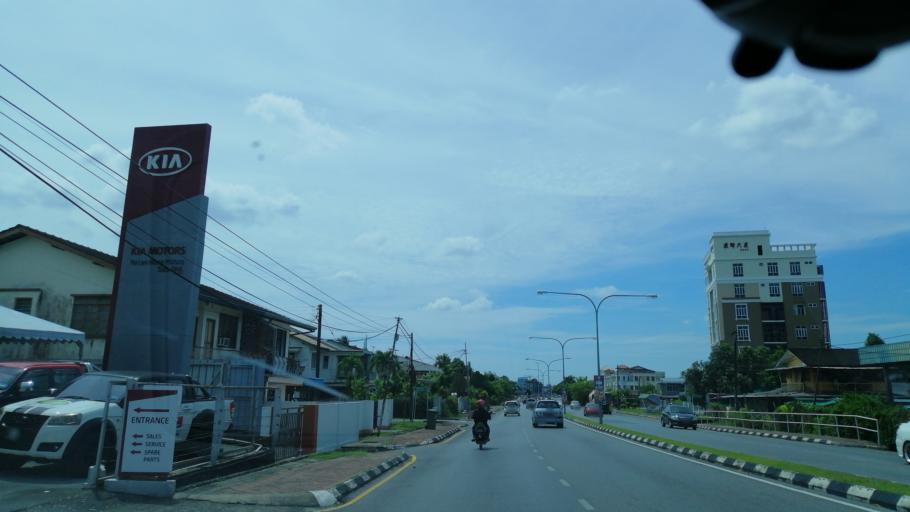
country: MY
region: Sarawak
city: Kuching
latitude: 1.5428
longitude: 110.3563
